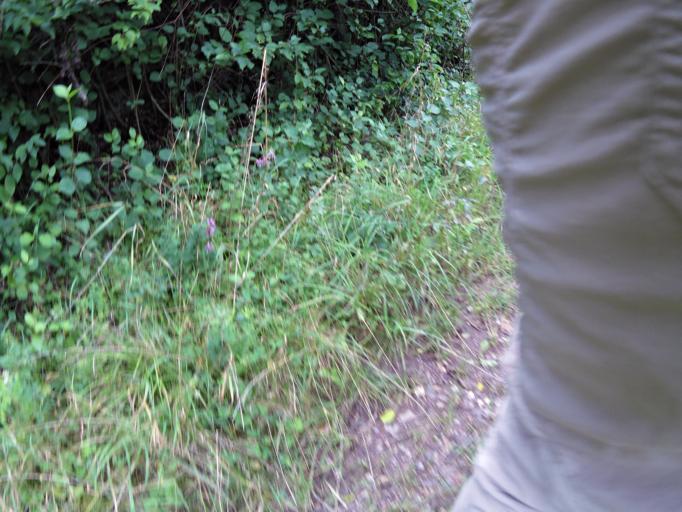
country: DE
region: Rheinland-Pfalz
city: Huffelsheim
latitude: 49.8150
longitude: 7.7940
